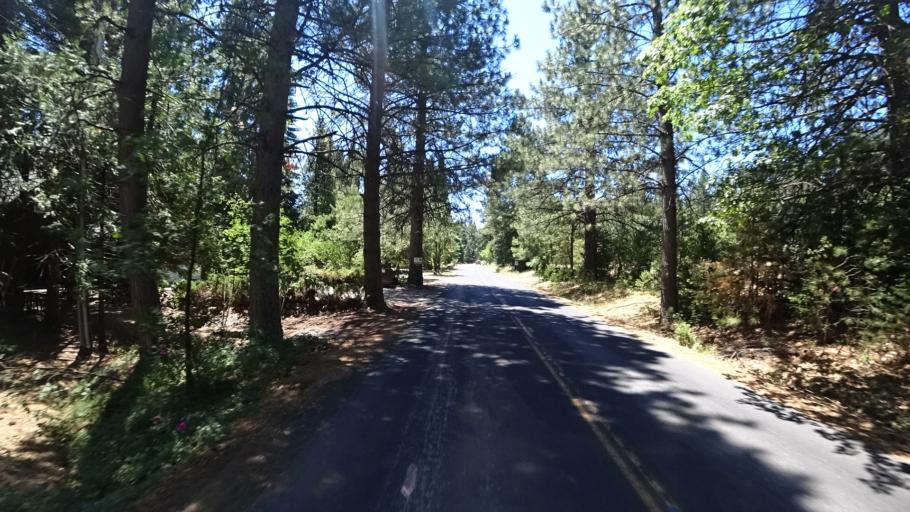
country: US
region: California
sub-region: Calaveras County
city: Arnold
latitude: 38.2525
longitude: -120.3316
